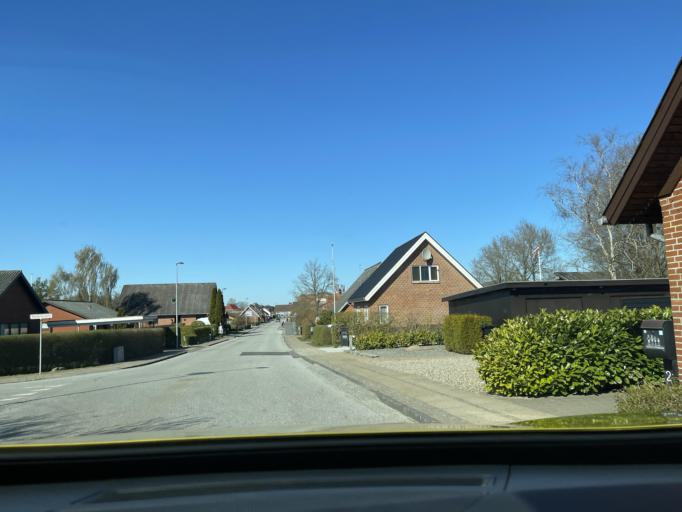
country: DK
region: Central Jutland
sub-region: Ikast-Brande Kommune
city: Bording Kirkeby
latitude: 56.1441
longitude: 9.2751
